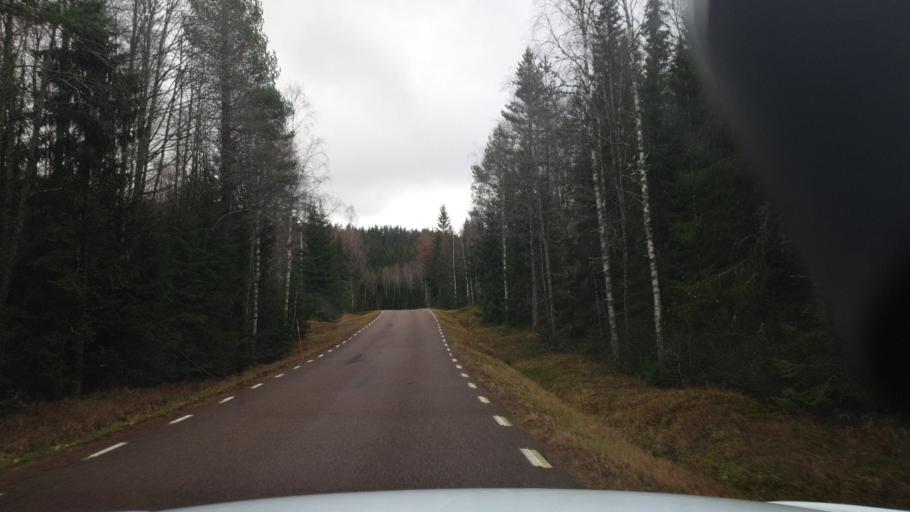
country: SE
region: Vaermland
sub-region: Arvika Kommun
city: Arvika
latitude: 59.8032
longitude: 12.8352
